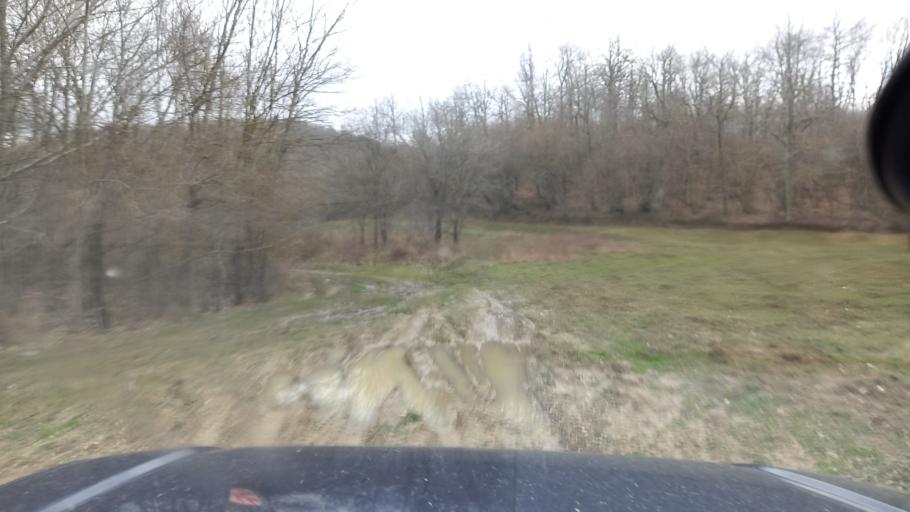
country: RU
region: Krasnodarskiy
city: Pshada
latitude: 44.4831
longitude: 38.4014
